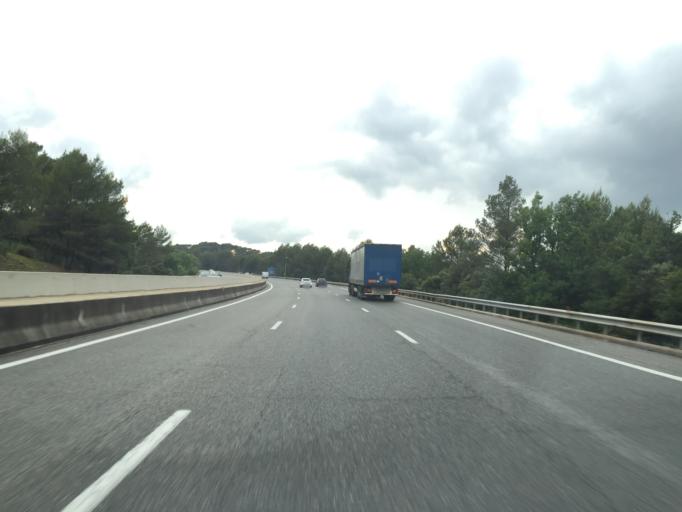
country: FR
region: Provence-Alpes-Cote d'Azur
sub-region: Departement du Var
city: Cabasse
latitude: 43.4051
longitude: 6.2102
